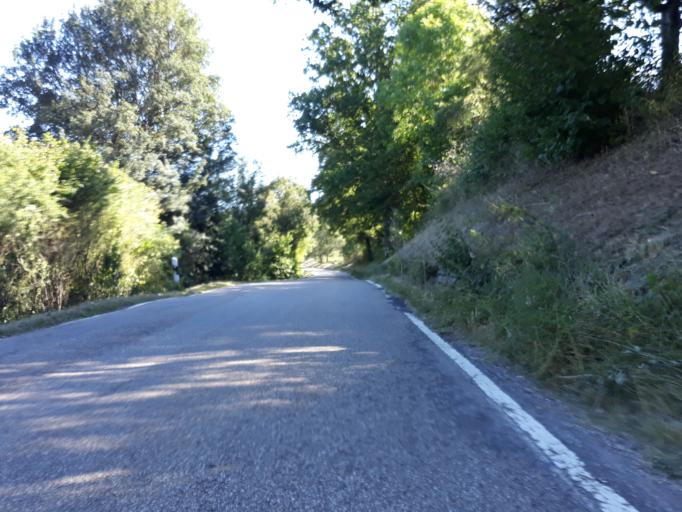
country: DE
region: Baden-Wuerttemberg
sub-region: Regierungsbezirk Stuttgart
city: Aidlingen
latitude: 48.6888
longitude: 8.8997
